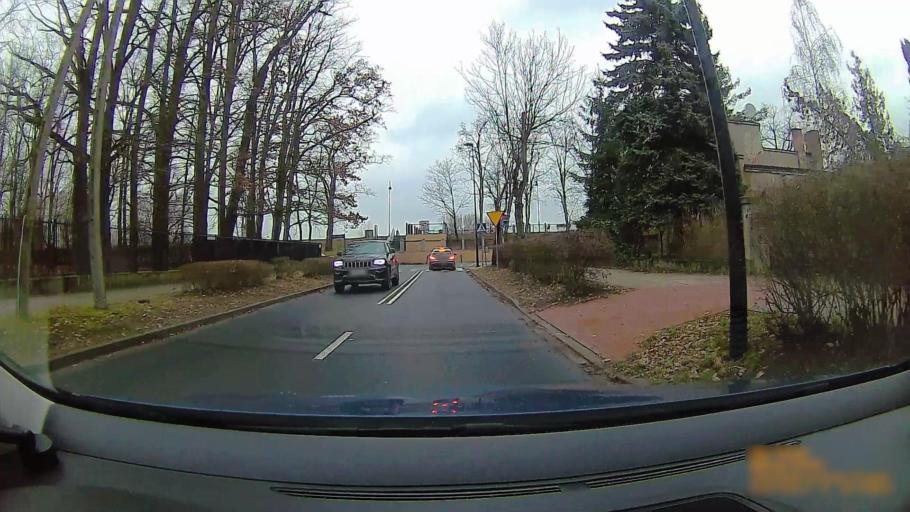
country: PL
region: Greater Poland Voivodeship
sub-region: Konin
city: Konin
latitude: 52.2118
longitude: 18.2464
